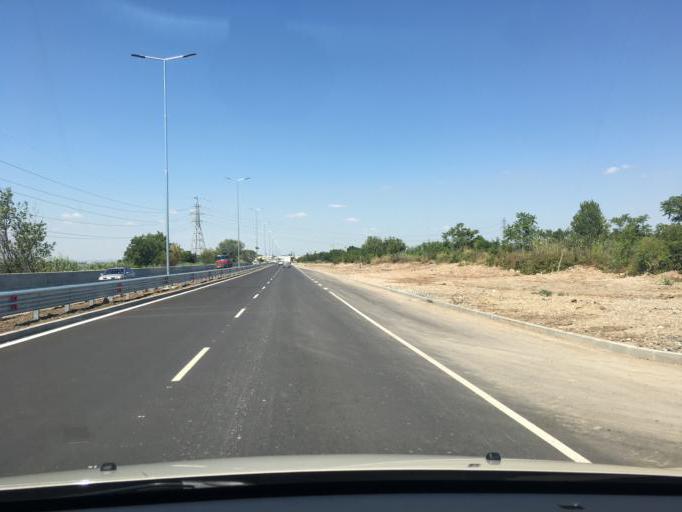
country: BG
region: Burgas
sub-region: Obshtina Burgas
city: Burgas
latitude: 42.5058
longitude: 27.4475
